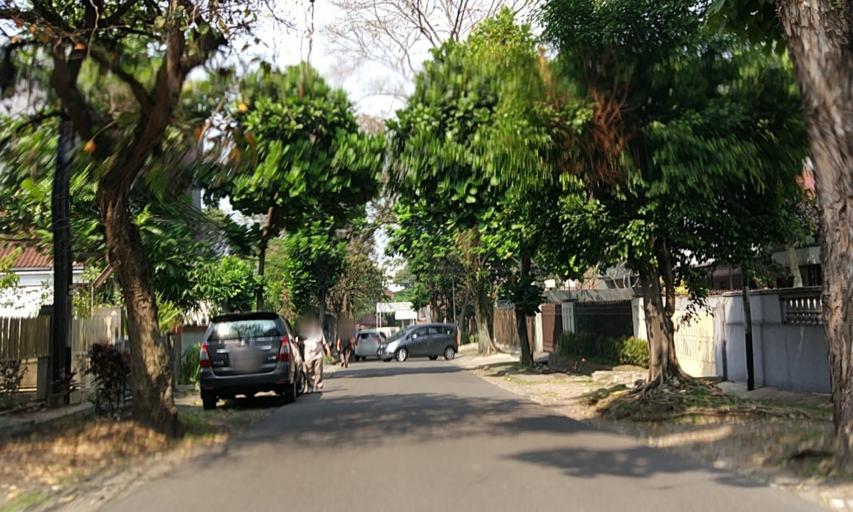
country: ID
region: West Java
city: Bandung
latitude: -6.9032
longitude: 107.5985
